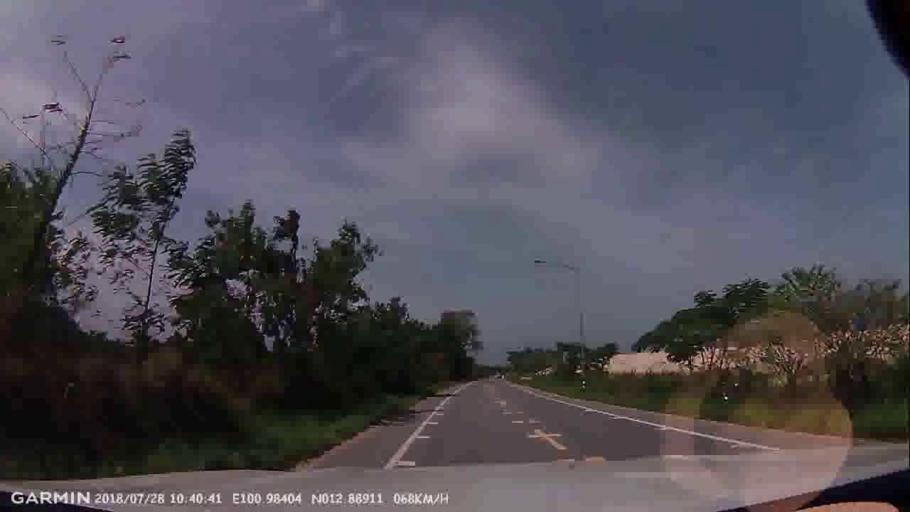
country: TH
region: Chon Buri
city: Phatthaya
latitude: 12.8889
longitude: 100.9840
